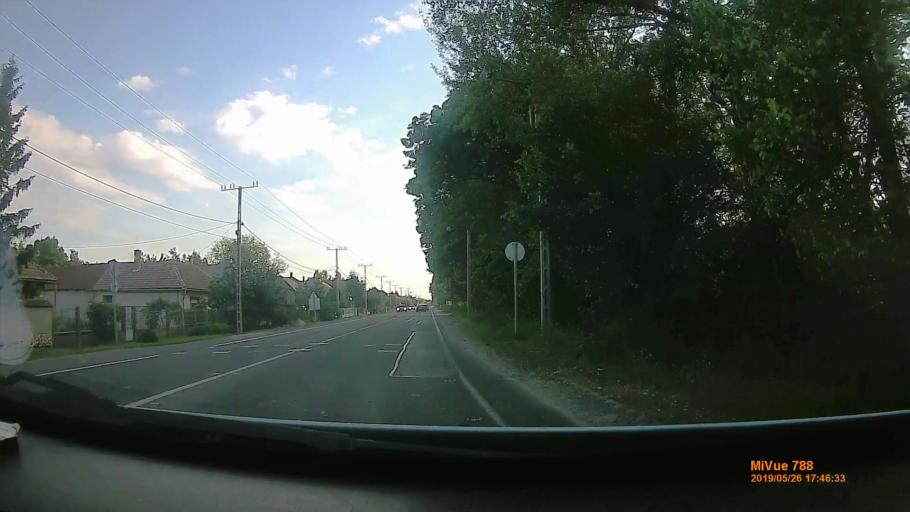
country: HU
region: Borsod-Abauj-Zemplen
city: Szikszo
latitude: 48.2077
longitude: 20.9382
